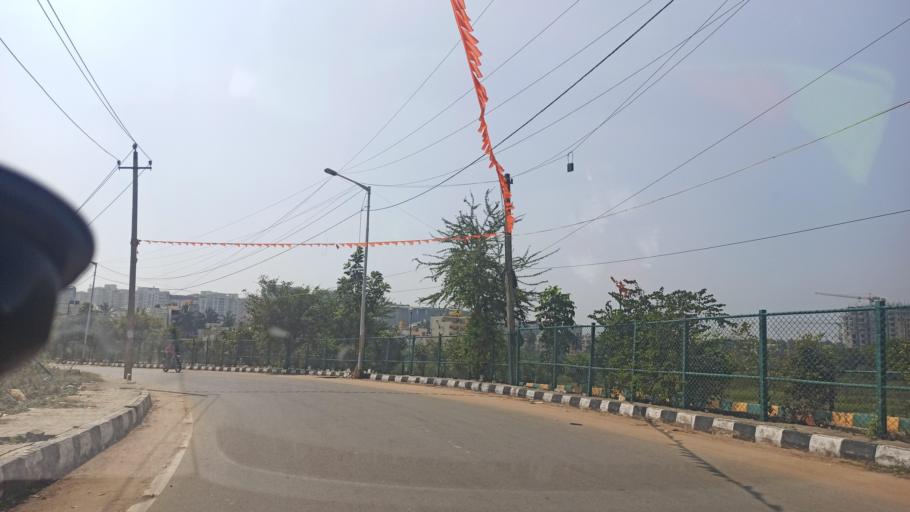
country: IN
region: Karnataka
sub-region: Bangalore Urban
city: Yelahanka
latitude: 13.0625
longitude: 77.5999
